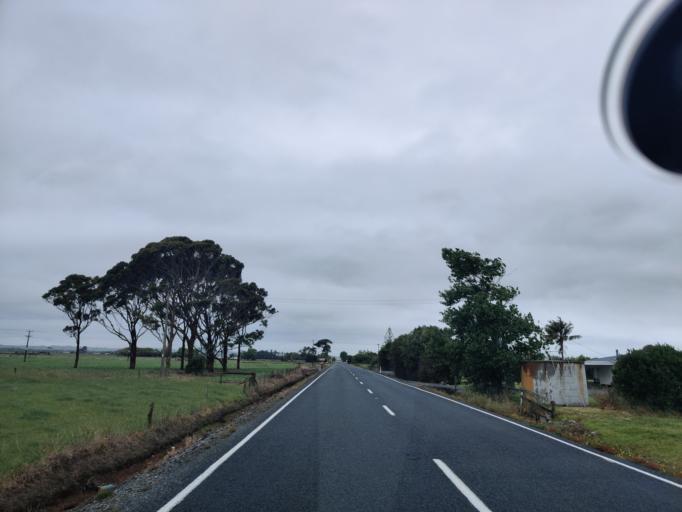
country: NZ
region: Northland
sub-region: Kaipara District
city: Dargaville
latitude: -36.1218
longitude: 173.9978
